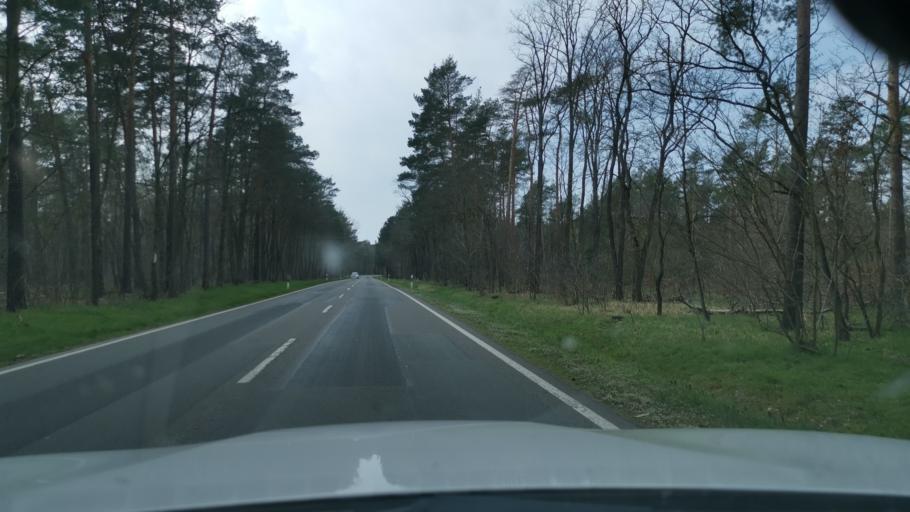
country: DE
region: Saxony
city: Lobnitz
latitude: 51.5610
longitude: 12.5066
